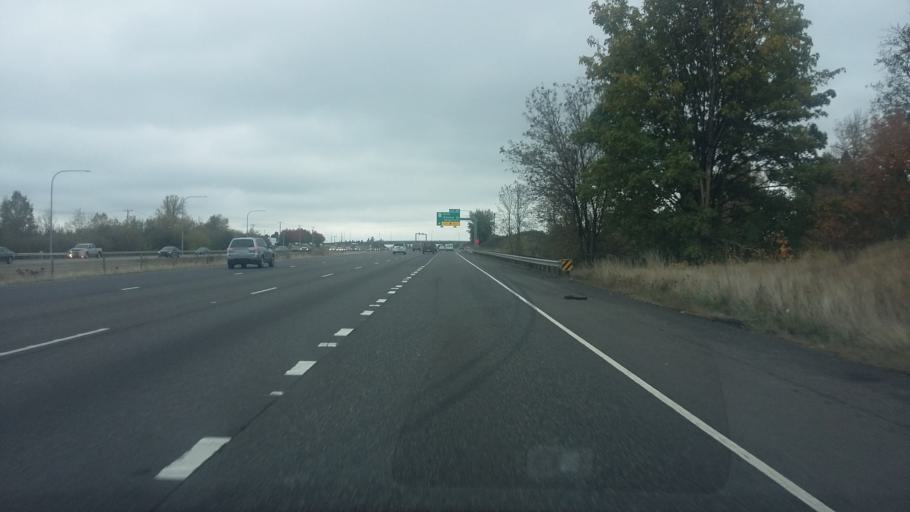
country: US
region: Washington
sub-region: Clark County
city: La Center
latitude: 45.8092
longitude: -122.6826
